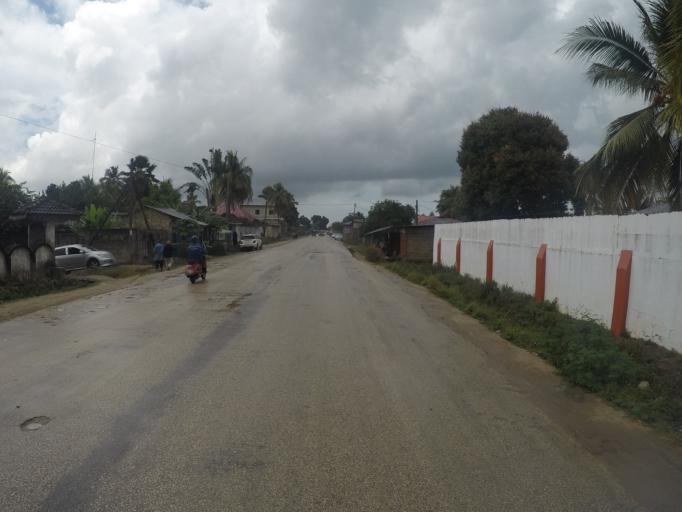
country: TZ
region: Zanzibar Urban/West
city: Zanzibar
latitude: -6.0946
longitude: 39.2191
